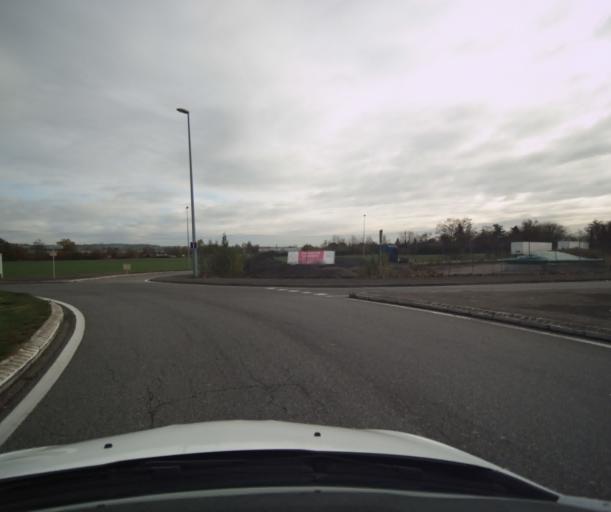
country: FR
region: Midi-Pyrenees
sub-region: Departement de la Haute-Garonne
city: Bruguieres
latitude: 43.7165
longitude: 1.4059
